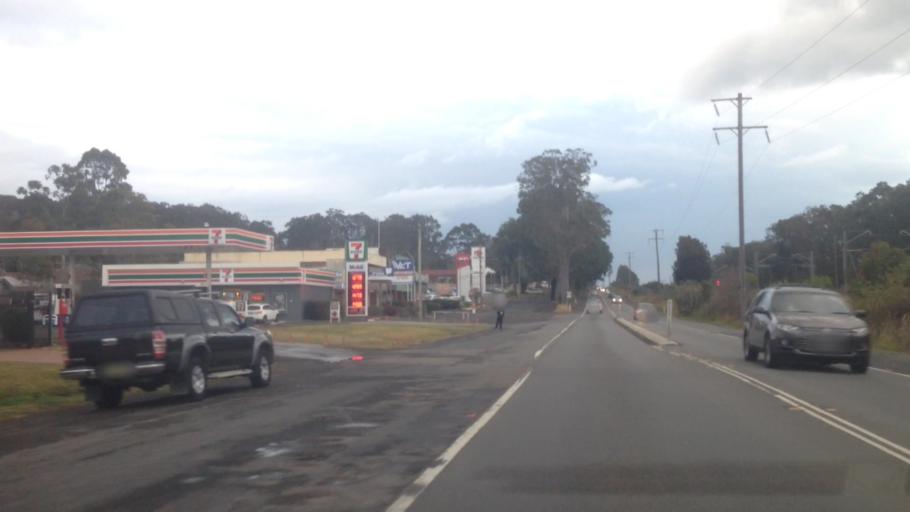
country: AU
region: New South Wales
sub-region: Wyong Shire
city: Jilliby
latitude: -33.2749
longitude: 151.4293
